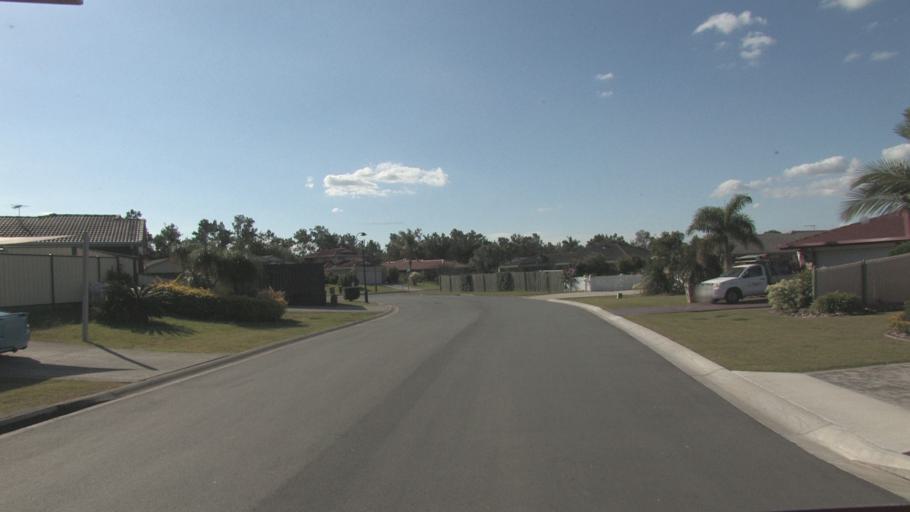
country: AU
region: Queensland
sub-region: Logan
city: Windaroo
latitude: -27.7497
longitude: 153.1944
